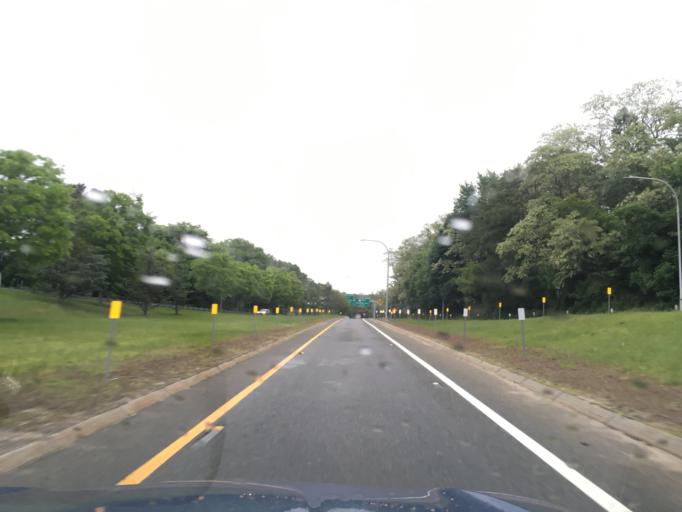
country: US
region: Rhode Island
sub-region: Providence County
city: Cranston
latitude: 41.7762
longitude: -71.4181
